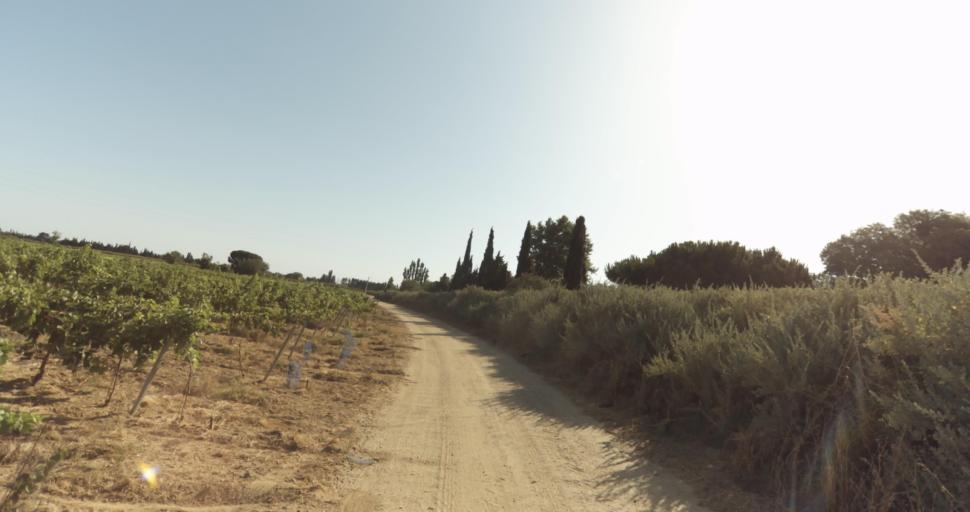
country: FR
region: Languedoc-Roussillon
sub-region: Departement des Pyrenees-Orientales
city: Alenya
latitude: 42.6471
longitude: 2.9740
